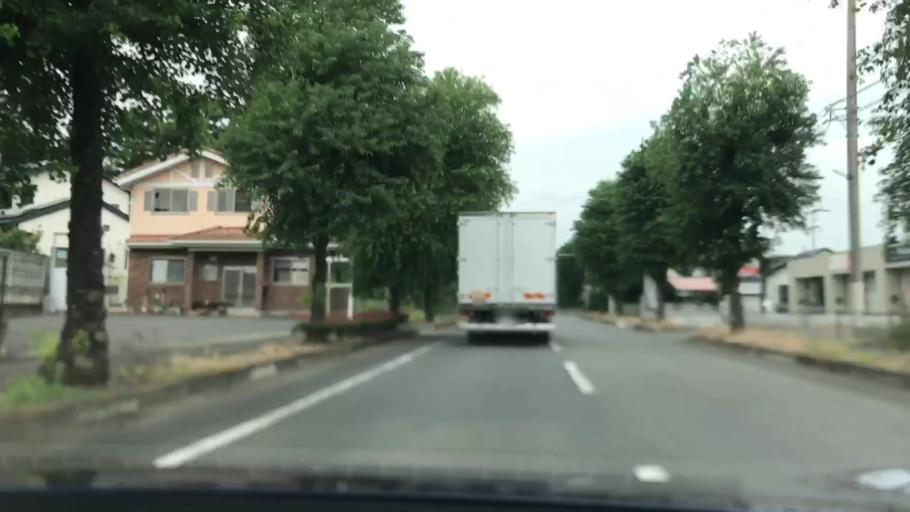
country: JP
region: Gunma
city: Isesaki
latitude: 36.3325
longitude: 139.1577
